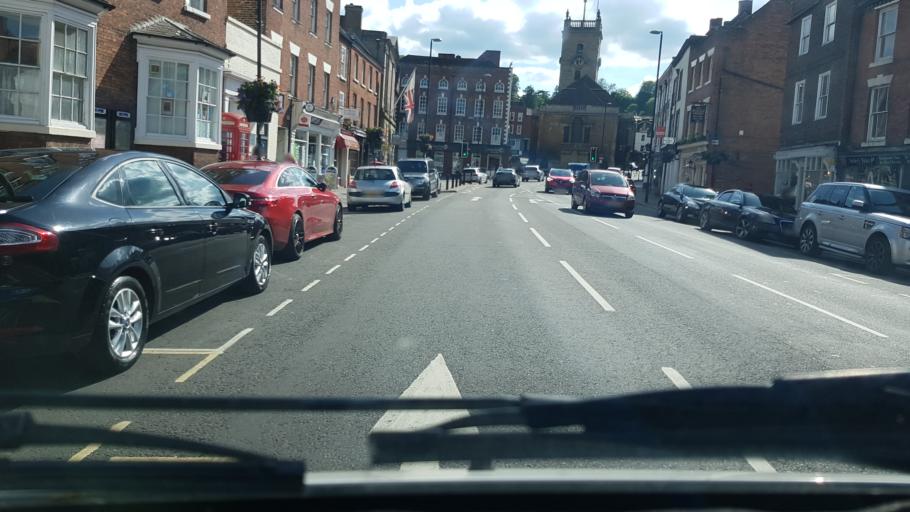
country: GB
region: England
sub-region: Worcestershire
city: Bewdley
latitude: 52.3761
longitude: -2.3144
